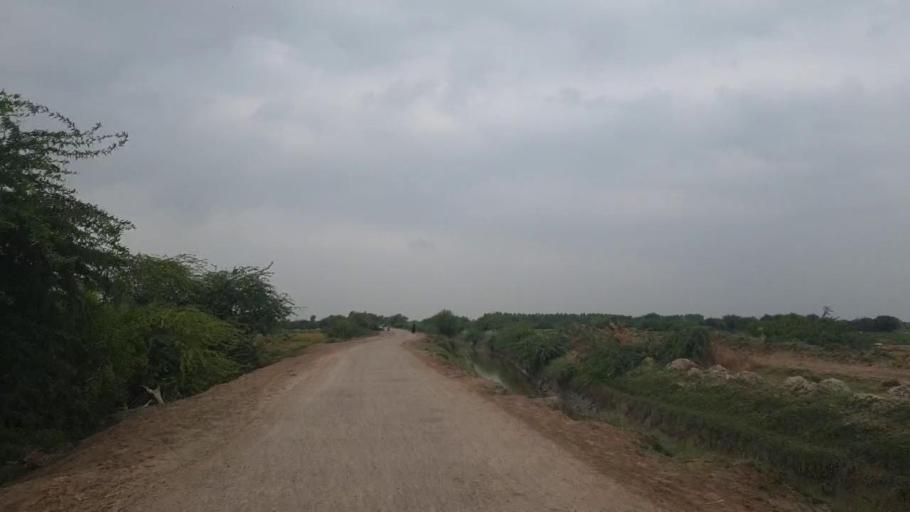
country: PK
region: Sindh
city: Badin
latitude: 24.6354
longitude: 68.6821
